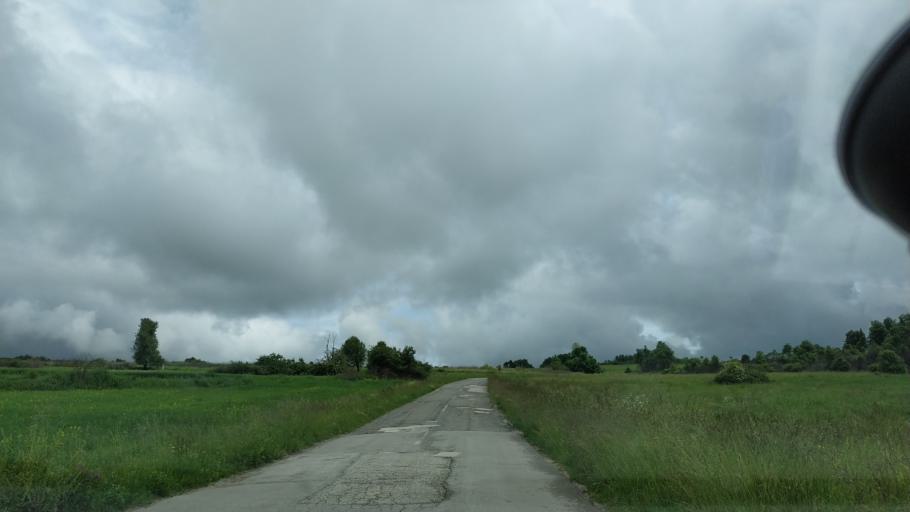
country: RS
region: Central Serbia
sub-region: Zajecarski Okrug
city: Soko Banja
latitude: 43.6910
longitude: 21.9326
